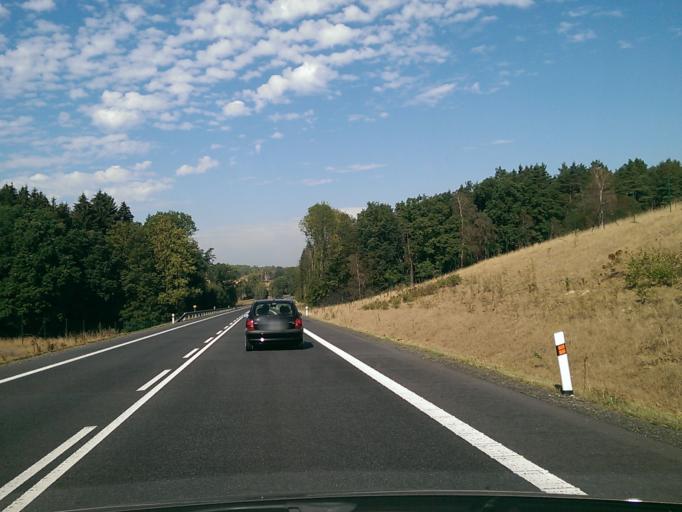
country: CZ
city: Chrastava
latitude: 50.8419
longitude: 14.9138
